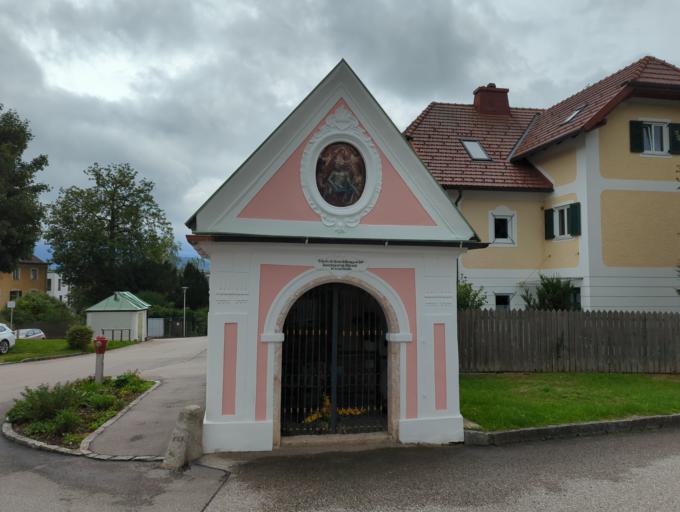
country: AT
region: Upper Austria
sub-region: Politischer Bezirk Gmunden
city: Gmunden
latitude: 47.9198
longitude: 13.8093
